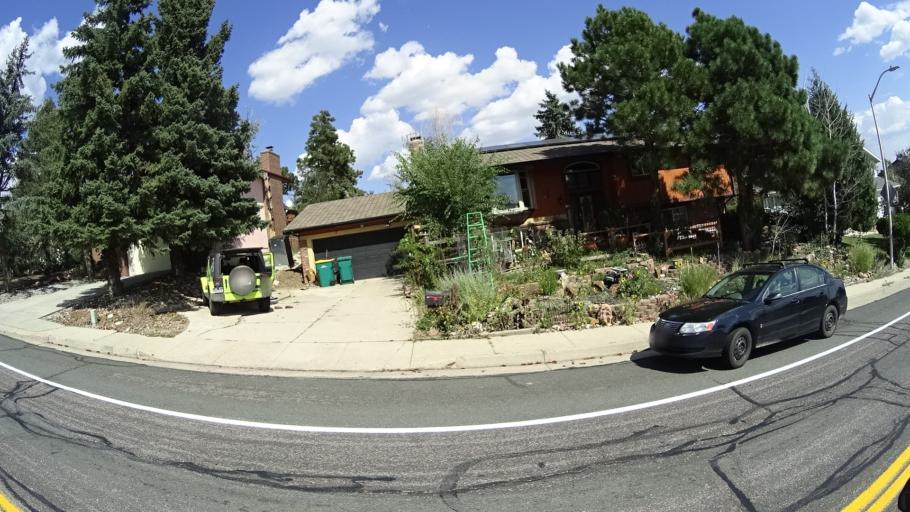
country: US
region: Colorado
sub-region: El Paso County
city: Cimarron Hills
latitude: 38.8701
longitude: -104.7362
